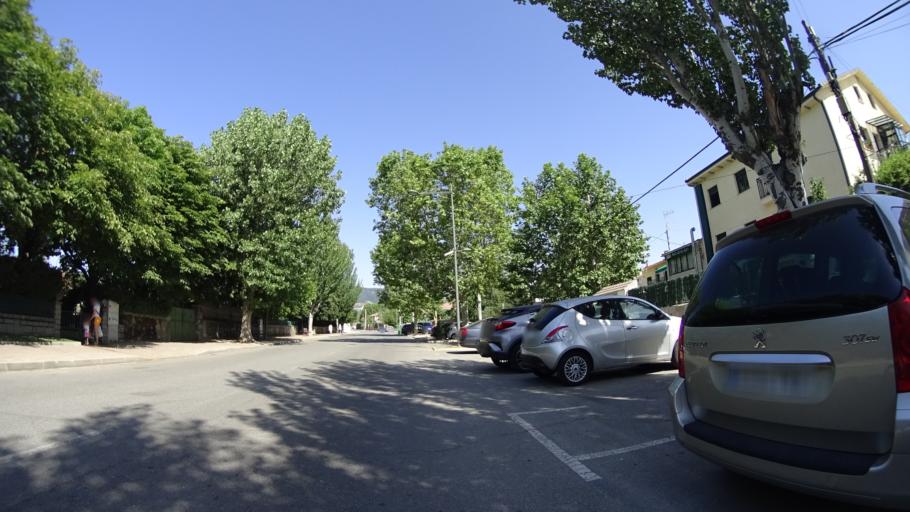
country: ES
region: Madrid
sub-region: Provincia de Madrid
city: Guadarrama
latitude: 40.6772
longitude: -4.0917
